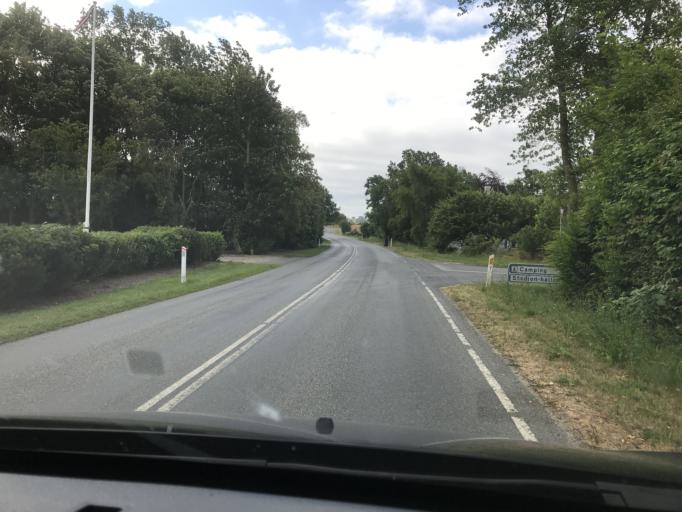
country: DK
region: South Denmark
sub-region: AEro Kommune
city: AEroskobing
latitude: 54.9328
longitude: 10.2645
